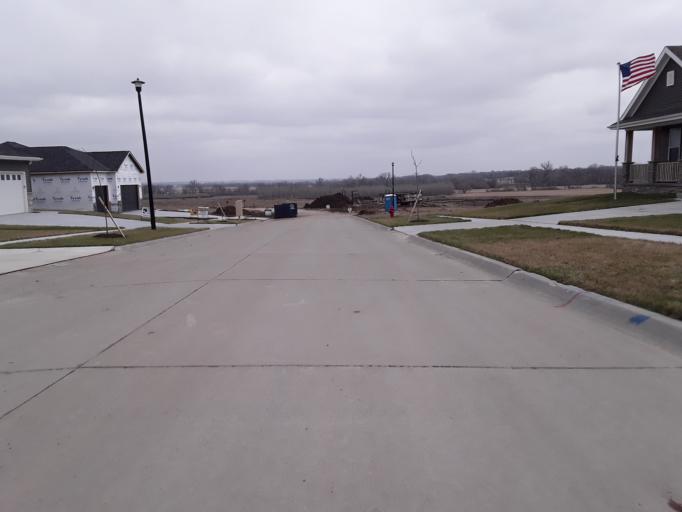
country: US
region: Nebraska
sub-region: Lancaster County
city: Lincoln
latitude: 40.8451
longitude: -96.5955
